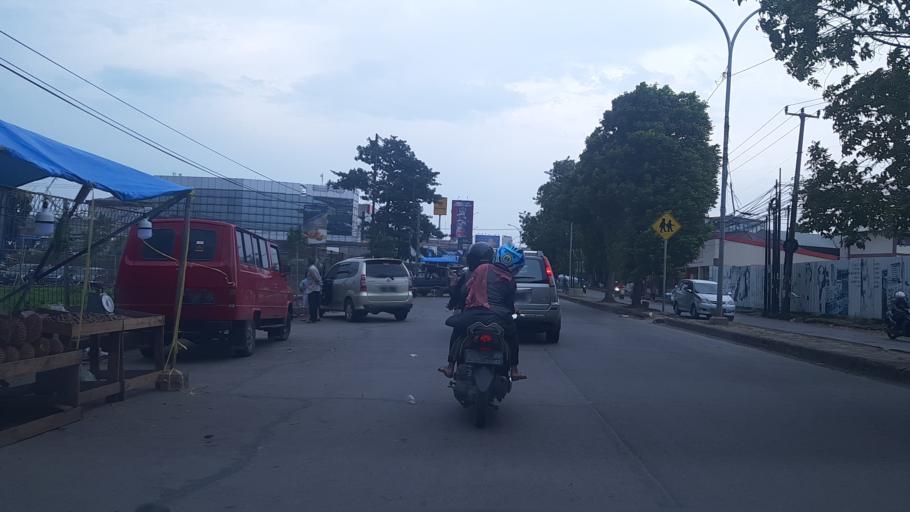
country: ID
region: West Java
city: Cibinong
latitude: -6.4675
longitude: 106.8576
